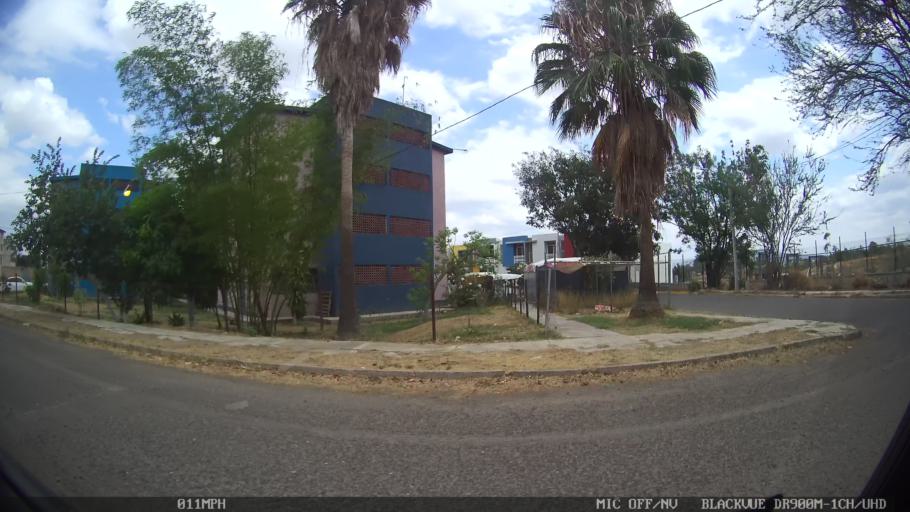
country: MX
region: Jalisco
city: Tonala
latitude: 20.6326
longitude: -103.2559
